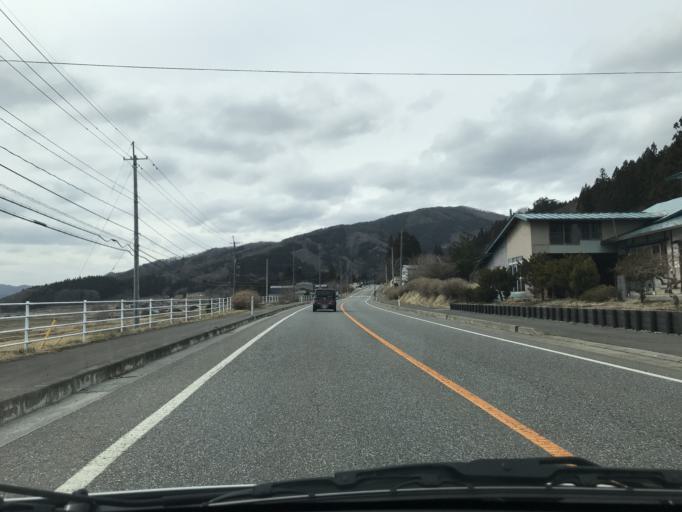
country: JP
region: Iwate
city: Tono
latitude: 39.3309
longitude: 141.4617
